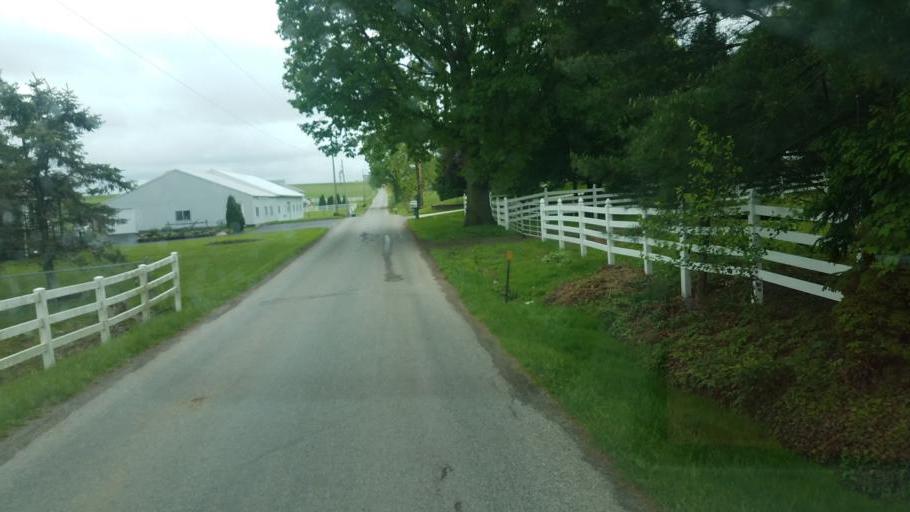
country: US
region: Ohio
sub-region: Wayne County
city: Apple Creek
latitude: 40.6314
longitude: -81.7905
